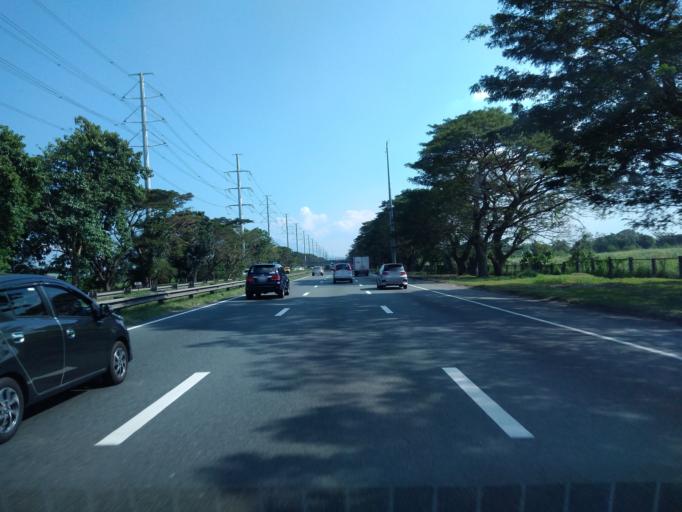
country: PH
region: Calabarzon
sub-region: Province of Laguna
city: Pulong Santa Cruz
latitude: 14.2622
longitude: 121.1001
